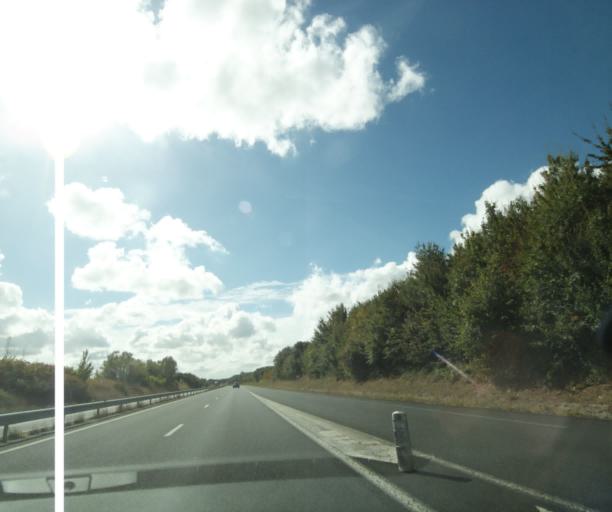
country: FR
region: Poitou-Charentes
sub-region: Departement de la Charente-Maritime
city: Saint-Savinien
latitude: 45.8657
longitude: -0.7323
